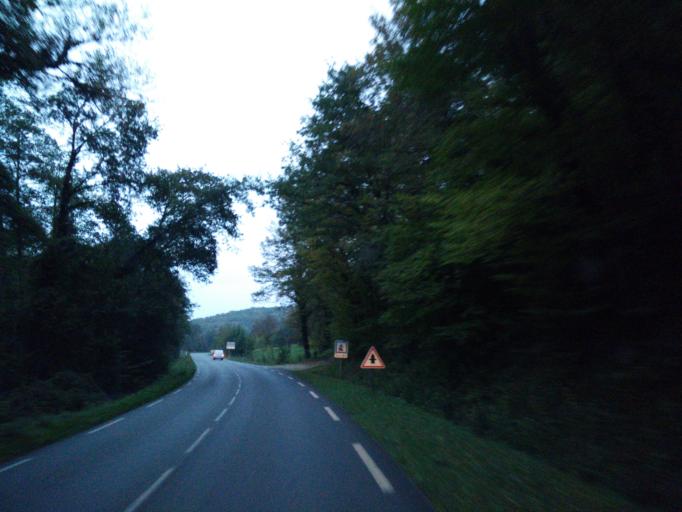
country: FR
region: Aquitaine
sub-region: Departement de la Dordogne
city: Saint-Cyprien
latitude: 44.9448
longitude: 1.0507
